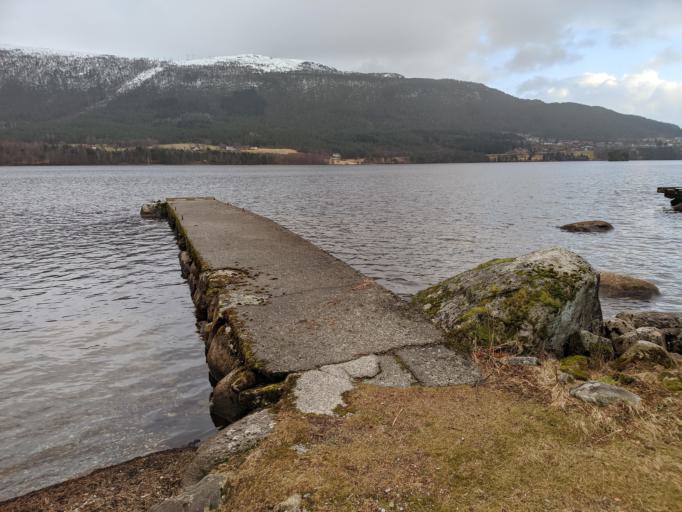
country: NO
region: Rogaland
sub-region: Vindafjord
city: Olen
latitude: 59.8588
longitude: 5.7557
